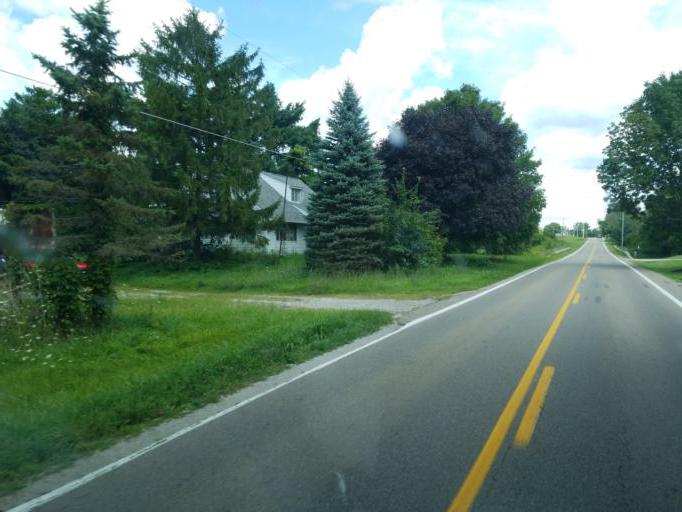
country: US
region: Ohio
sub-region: Knox County
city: Centerburg
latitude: 40.3380
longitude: -82.7969
